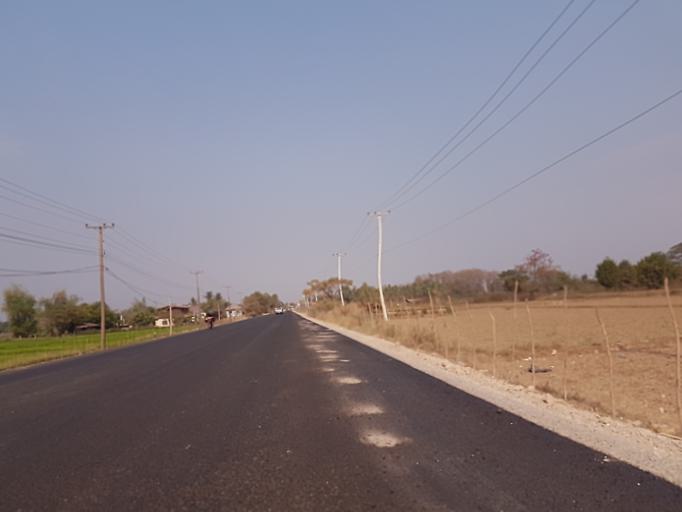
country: TH
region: Nong Khai
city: Nong Khai
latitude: 17.9282
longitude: 102.7724
